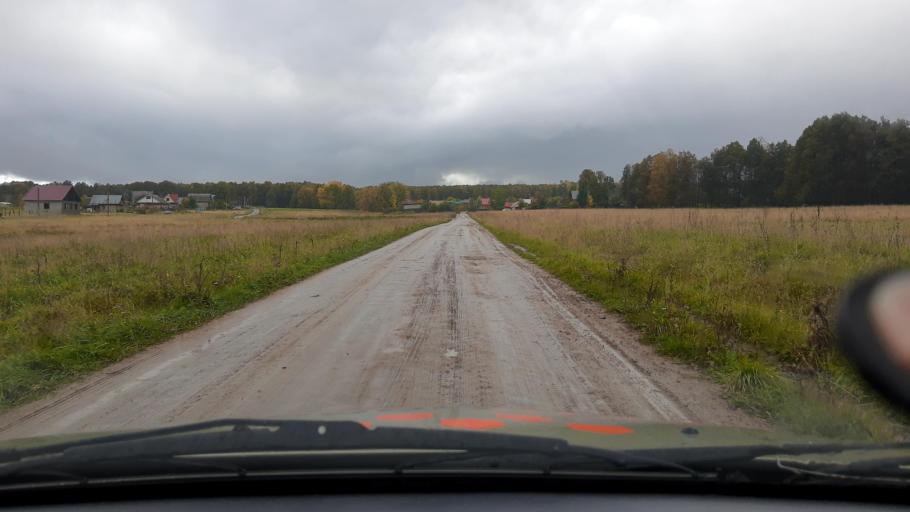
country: RU
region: Bashkortostan
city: Kudeyevskiy
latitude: 54.8784
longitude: 56.6302
